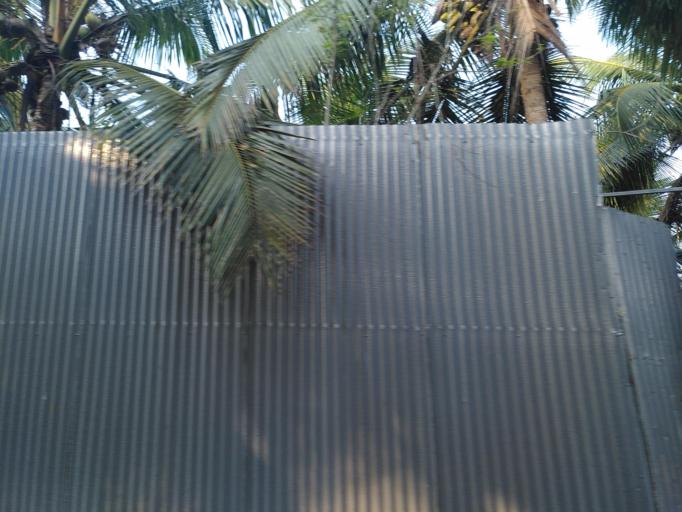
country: IN
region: Kerala
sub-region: Alappuzha
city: Arukutti
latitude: 9.9232
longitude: 76.3295
